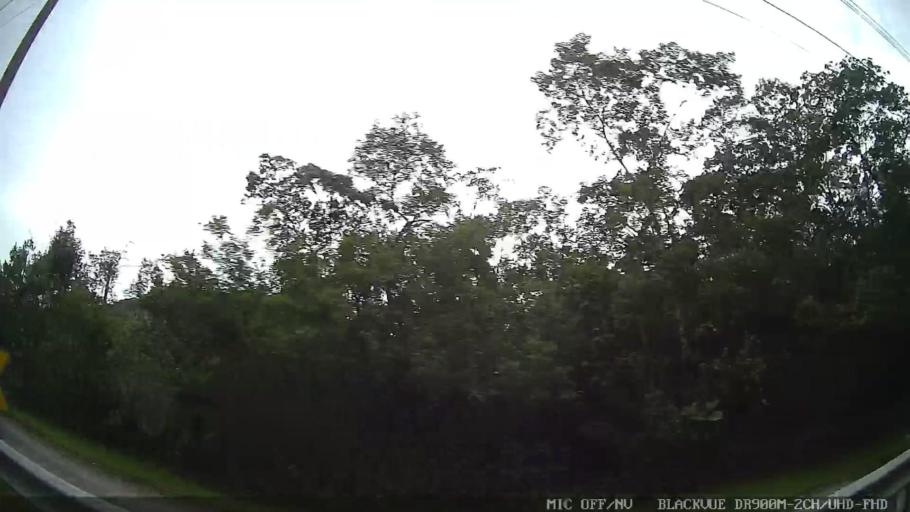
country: BR
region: Sao Paulo
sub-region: Caraguatatuba
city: Caraguatatuba
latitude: -23.5854
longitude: -45.4561
